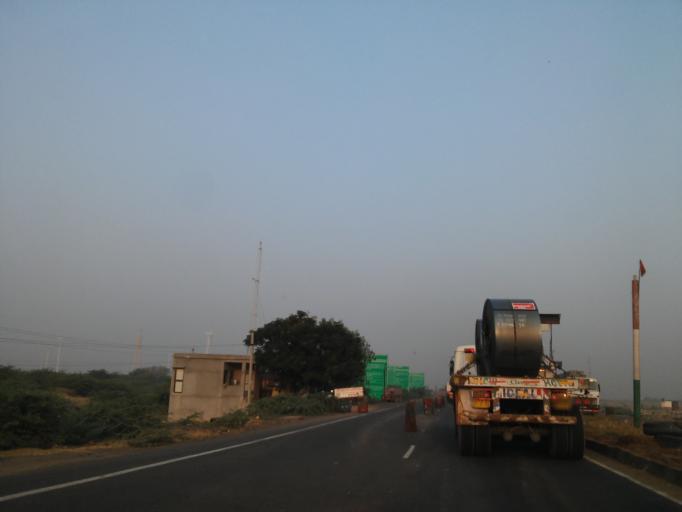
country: IN
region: Gujarat
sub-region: Kachchh
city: Rapar
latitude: 23.2317
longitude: 70.6930
